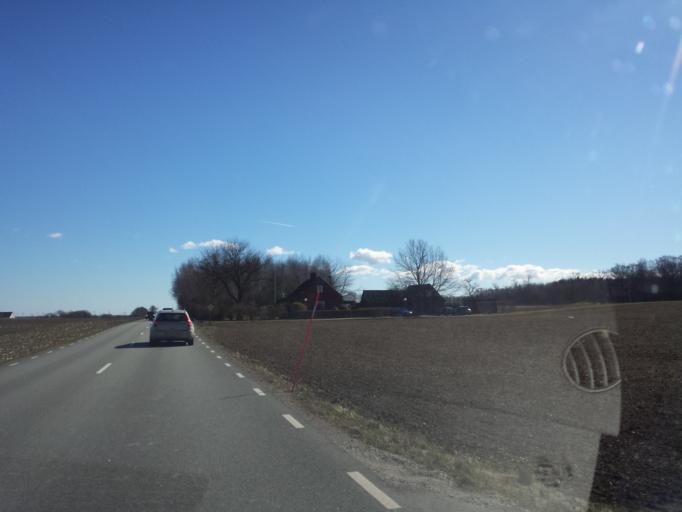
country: SE
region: Skane
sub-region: Sjobo Kommun
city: Sjoebo
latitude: 55.6132
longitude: 13.7865
